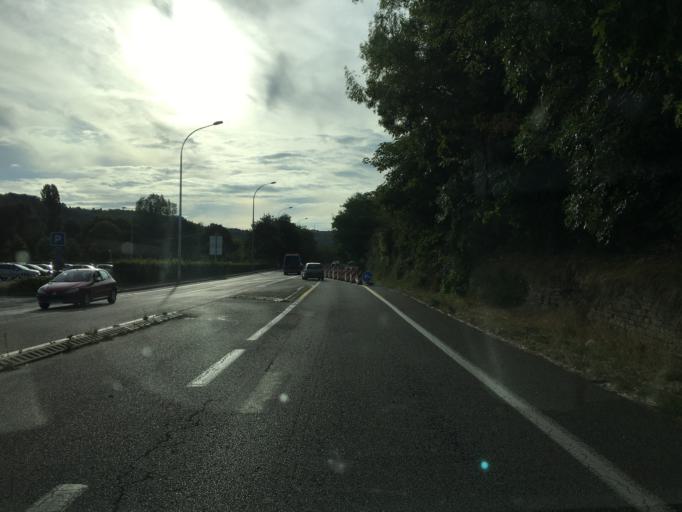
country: FR
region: Bourgogne
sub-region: Departement de la Cote-d'Or
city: Talant
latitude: 47.3300
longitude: 4.9985
